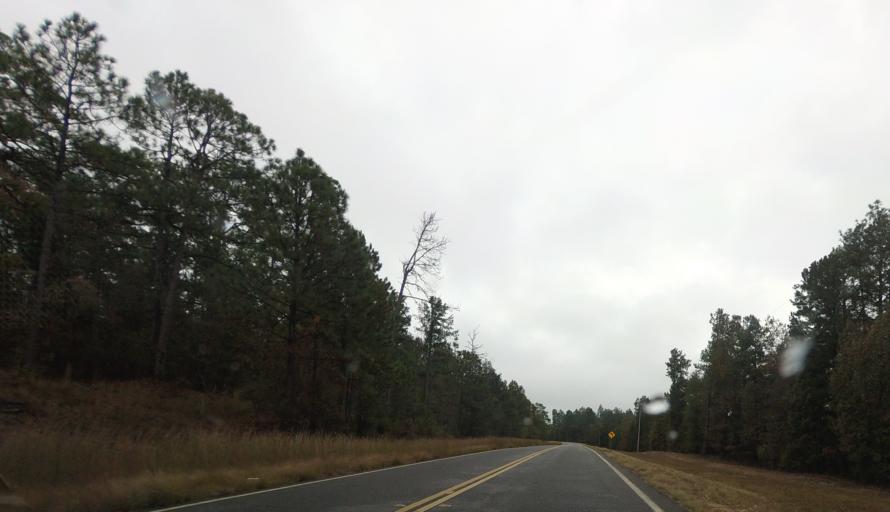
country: US
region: Georgia
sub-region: Taylor County
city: Butler
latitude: 32.4431
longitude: -84.3658
